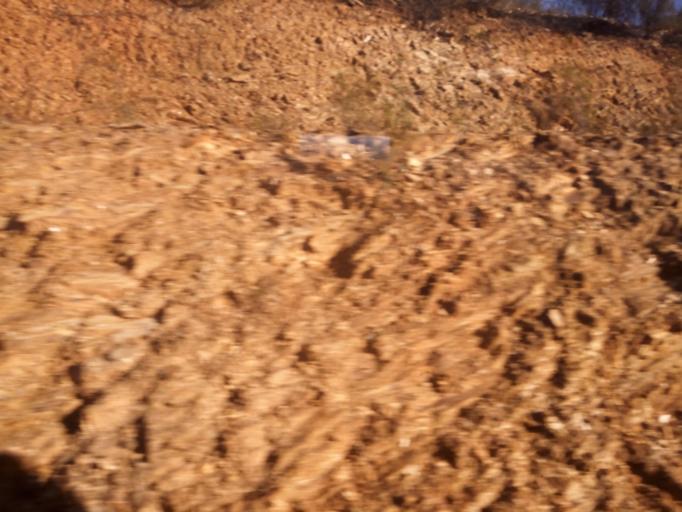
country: PT
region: Beja
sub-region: Odemira
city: Odemira
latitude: 37.5693
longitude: -8.4858
